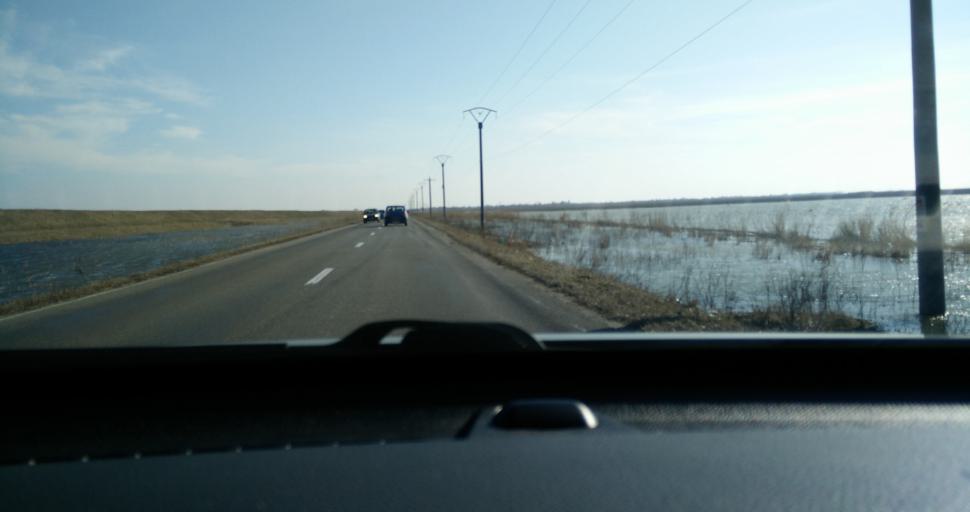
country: RO
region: Vrancea
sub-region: Comuna Nanesti
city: Nanesti
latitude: 45.5686
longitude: 27.4988
